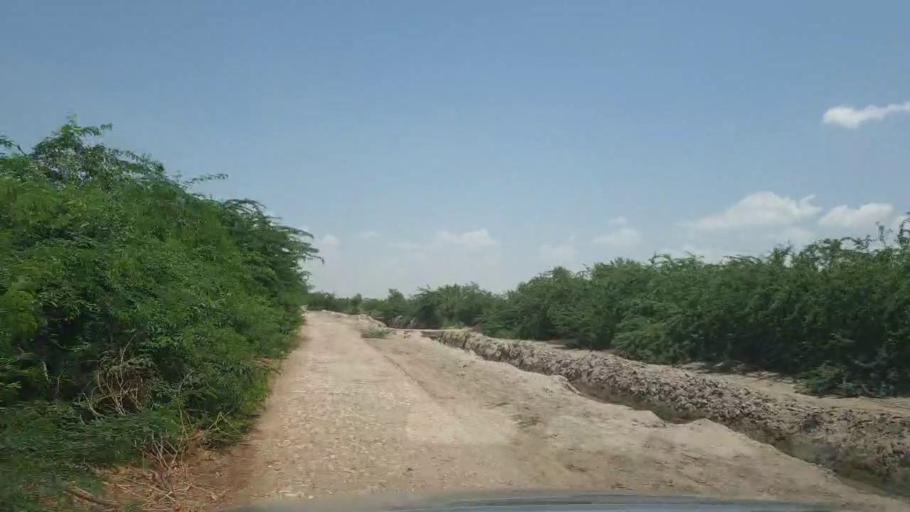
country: PK
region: Sindh
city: Kot Diji
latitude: 27.2924
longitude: 69.0671
